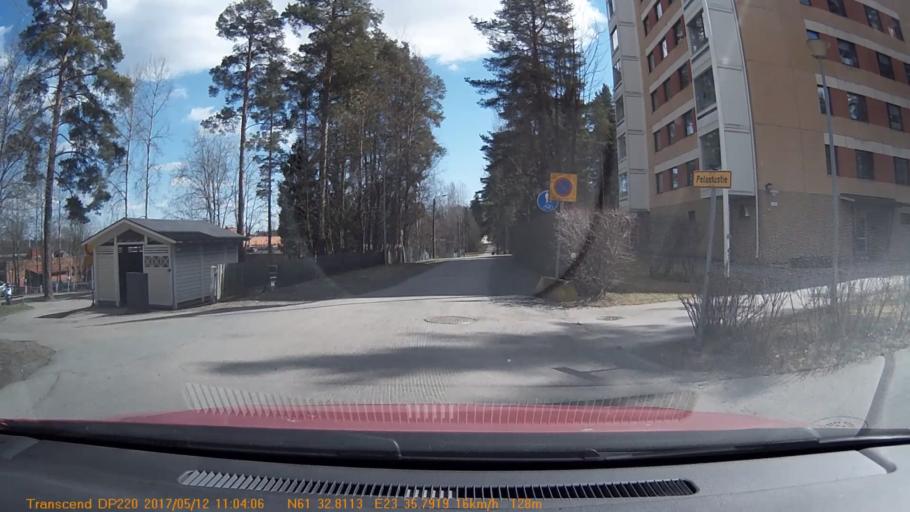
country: FI
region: Pirkanmaa
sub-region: Tampere
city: Yloejaervi
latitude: 61.5469
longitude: 23.5966
